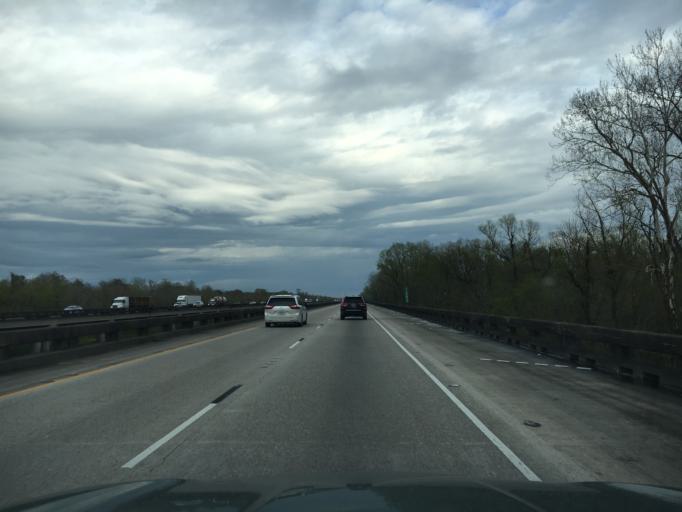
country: US
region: Louisiana
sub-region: Iberville Parish
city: Maringouin
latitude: 30.3699
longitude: -91.6205
